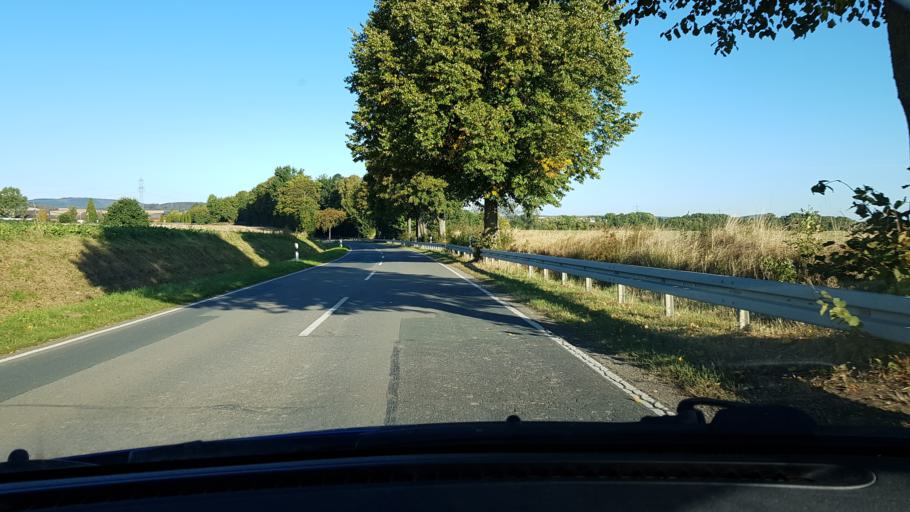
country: DE
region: Lower Saxony
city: Hulsede
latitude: 52.2553
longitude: 9.3613
